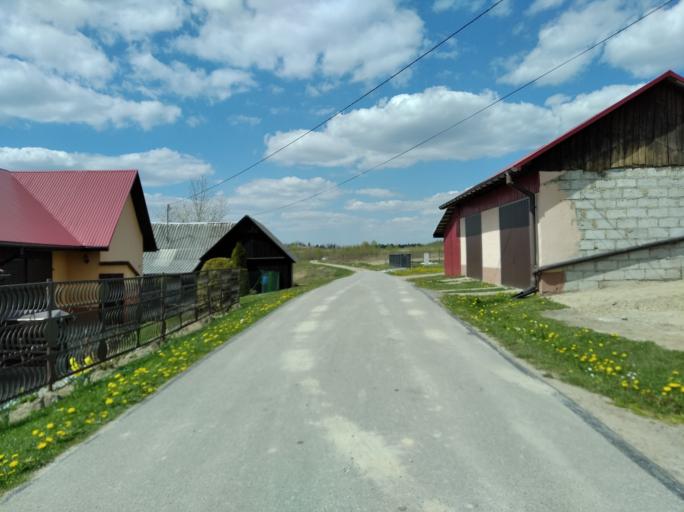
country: PL
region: Subcarpathian Voivodeship
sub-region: Powiat brzozowski
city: Jablonka
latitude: 49.7390
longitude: 22.0908
